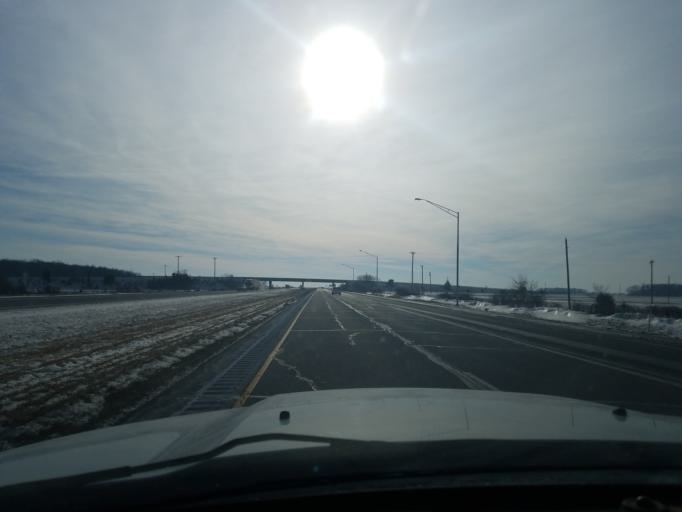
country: US
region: Indiana
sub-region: Huntington County
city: Warren
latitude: 40.7437
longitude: -85.4102
